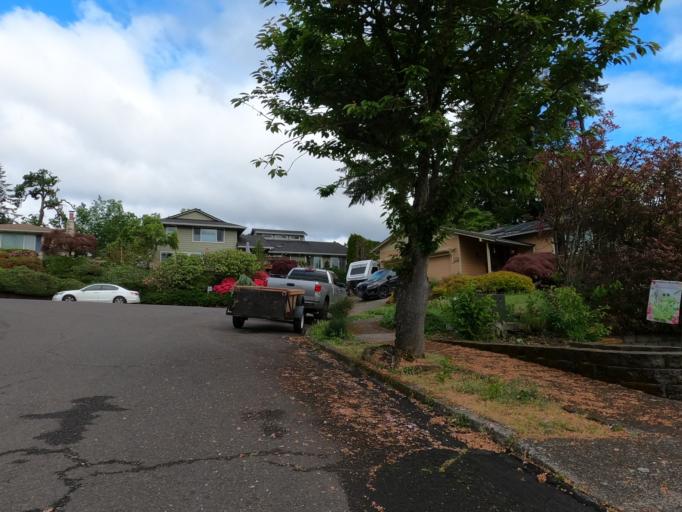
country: US
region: Oregon
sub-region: Clackamas County
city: Gladstone
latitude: 45.3963
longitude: -122.5902
